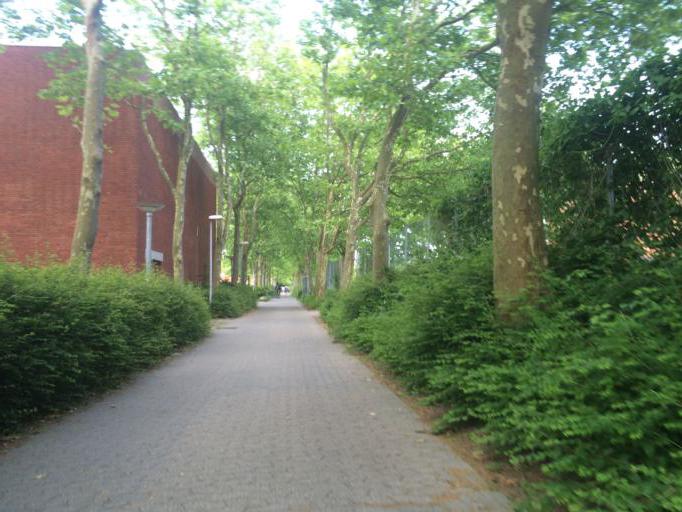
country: DK
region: Capital Region
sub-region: Tarnby Kommune
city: Tarnby
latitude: 55.6323
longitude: 12.6262
